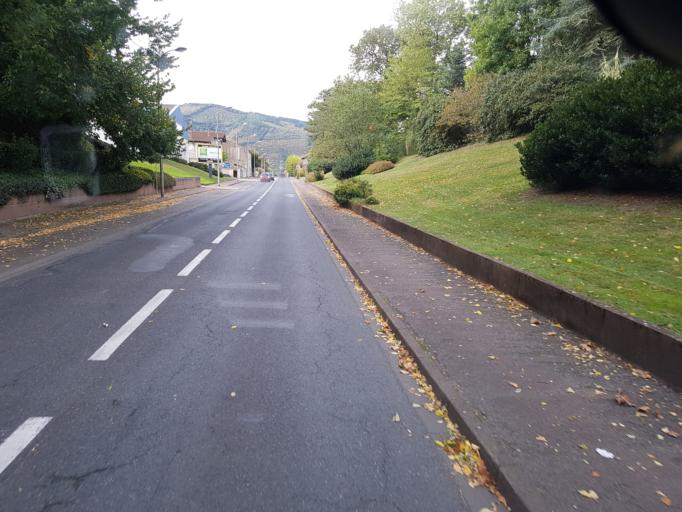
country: FR
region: Midi-Pyrenees
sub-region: Departement du Tarn
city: Mazamet
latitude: 43.4987
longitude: 2.3851
